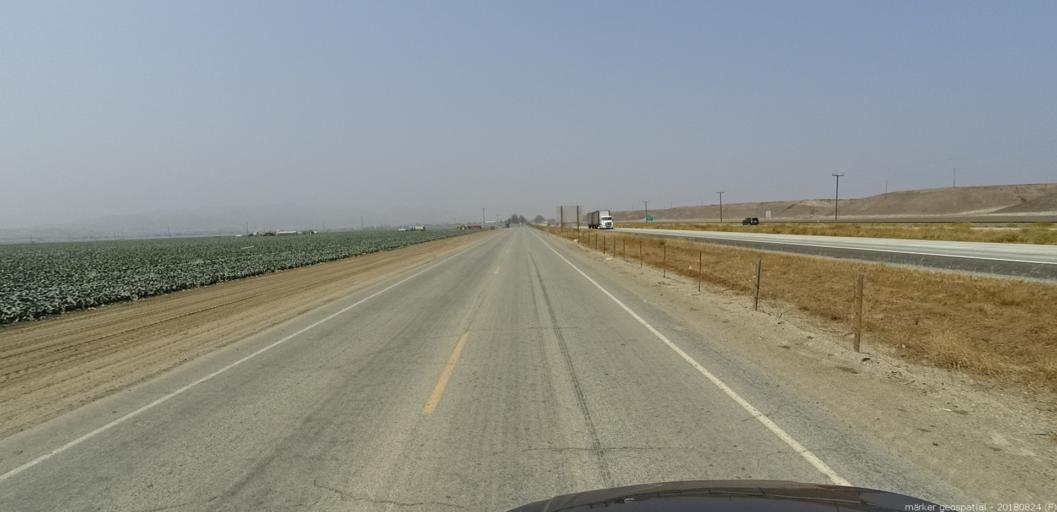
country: US
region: California
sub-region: Monterey County
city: King City
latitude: 36.1953
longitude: -121.0947
